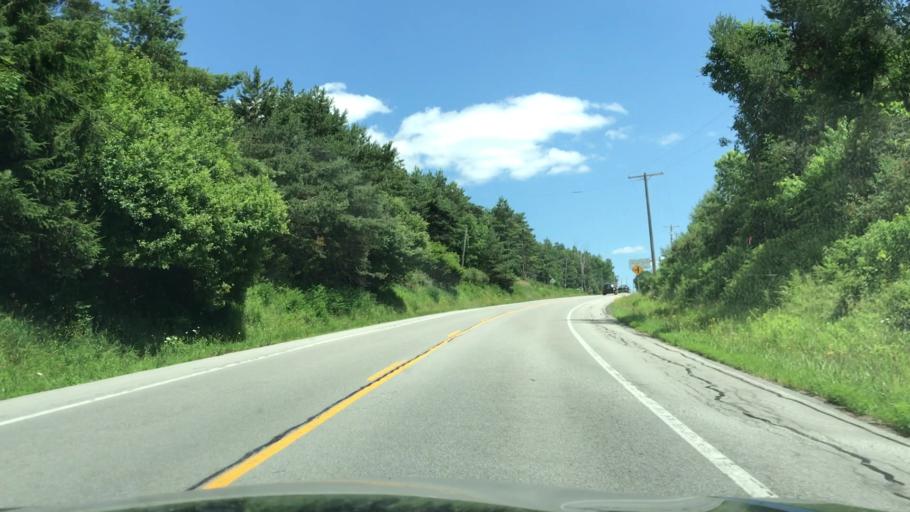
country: US
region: New York
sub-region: Wyoming County
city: Warsaw
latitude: 42.7489
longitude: -78.2384
